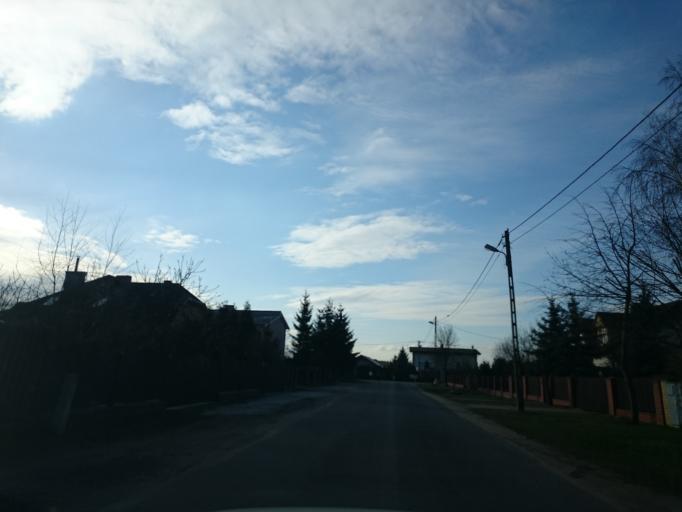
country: PL
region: Kujawsko-Pomorskie
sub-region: Powiat torunski
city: Lubicz Gorny
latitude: 53.0328
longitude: 18.7790
